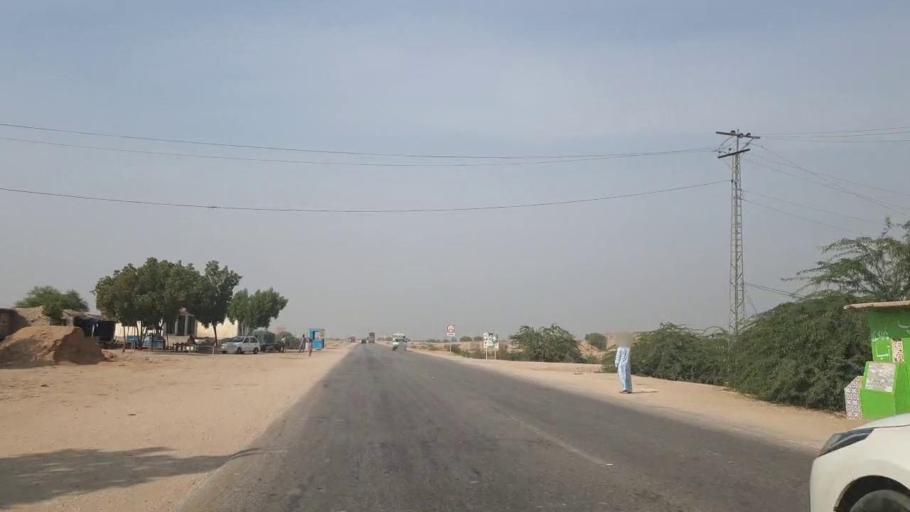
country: PK
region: Sindh
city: Sann
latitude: 26.0882
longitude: 68.0911
